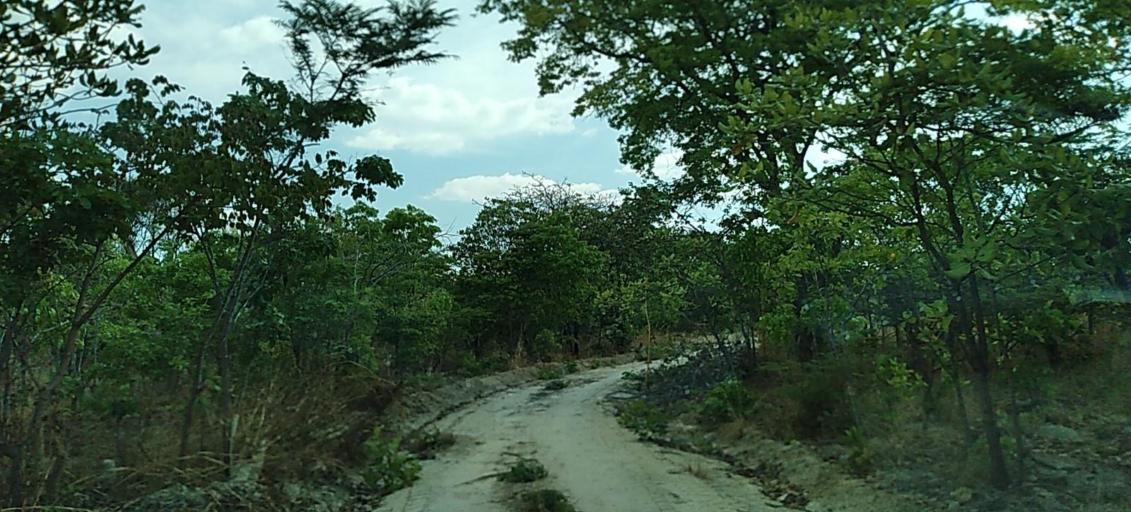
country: ZM
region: Copperbelt
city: Chililabombwe
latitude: -12.3365
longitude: 27.7816
